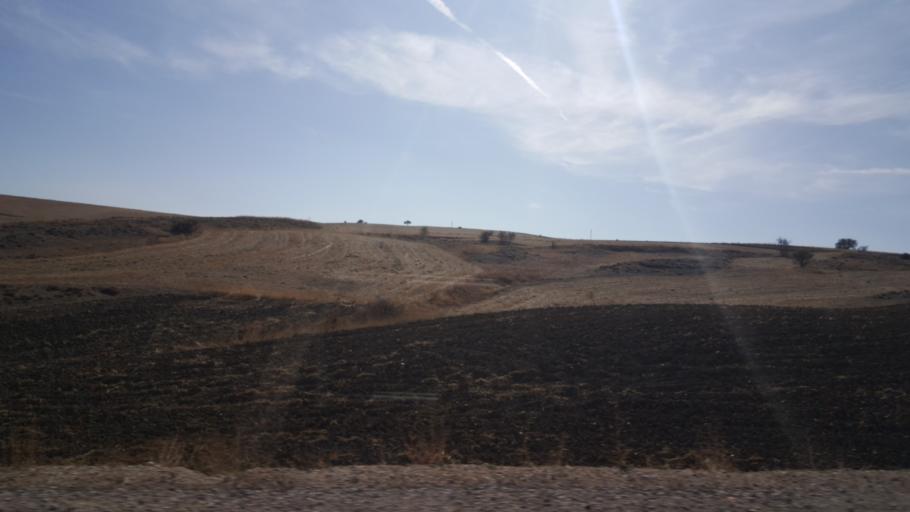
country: TR
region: Ankara
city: Haymana
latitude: 39.4269
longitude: 32.5587
